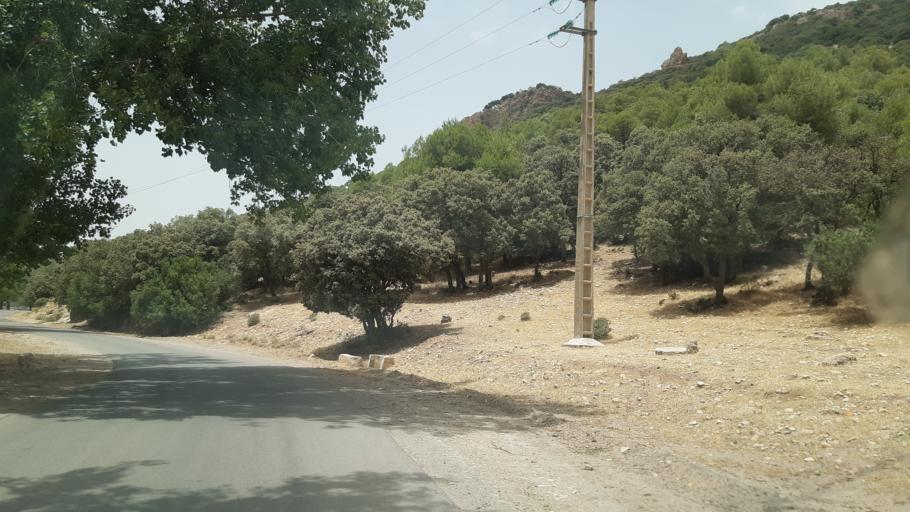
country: MA
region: Meknes-Tafilalet
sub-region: Ifrane
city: Ifrane
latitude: 33.6548
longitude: -5.0349
